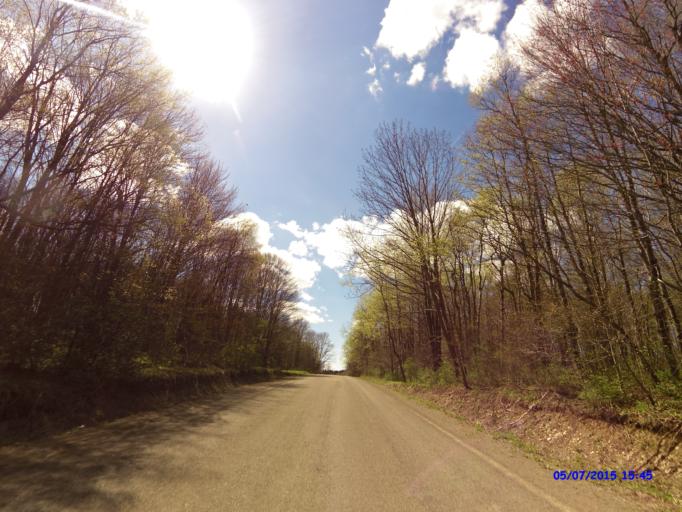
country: US
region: New York
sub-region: Cattaraugus County
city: Franklinville
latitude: 42.3149
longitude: -78.5539
